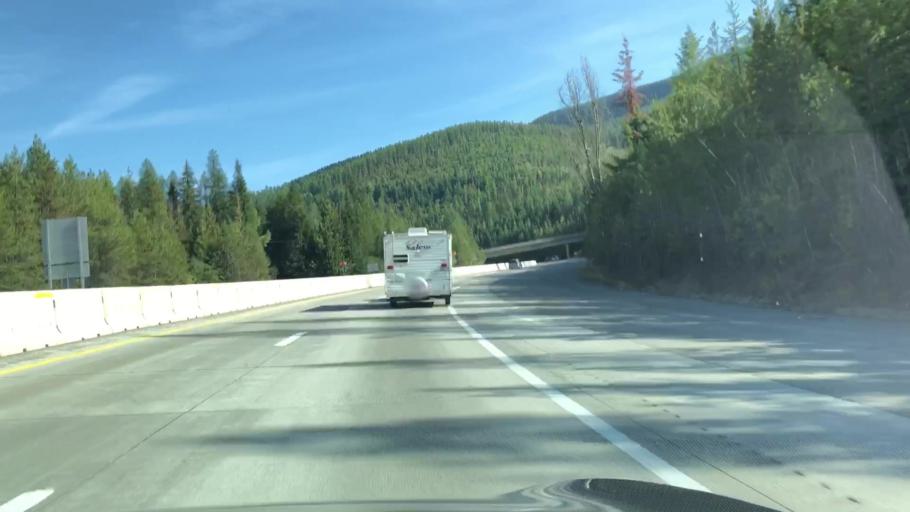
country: US
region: Idaho
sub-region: Shoshone County
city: Wallace
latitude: 47.4688
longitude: -115.7609
